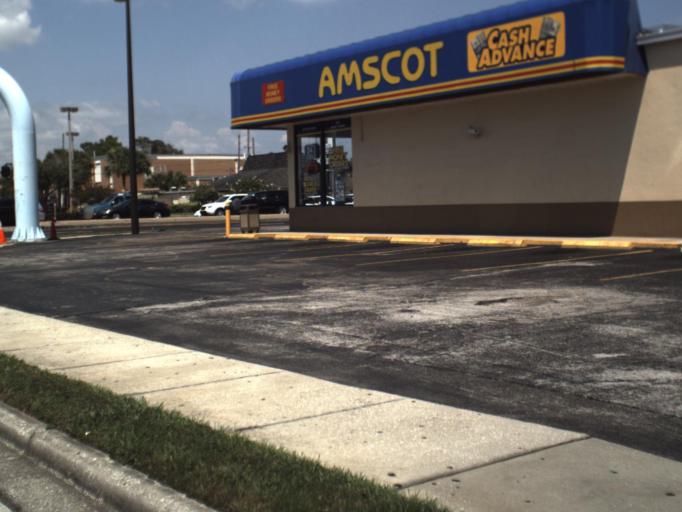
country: US
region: Florida
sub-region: Pinellas County
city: Kenneth City
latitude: 27.8386
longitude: -82.7284
